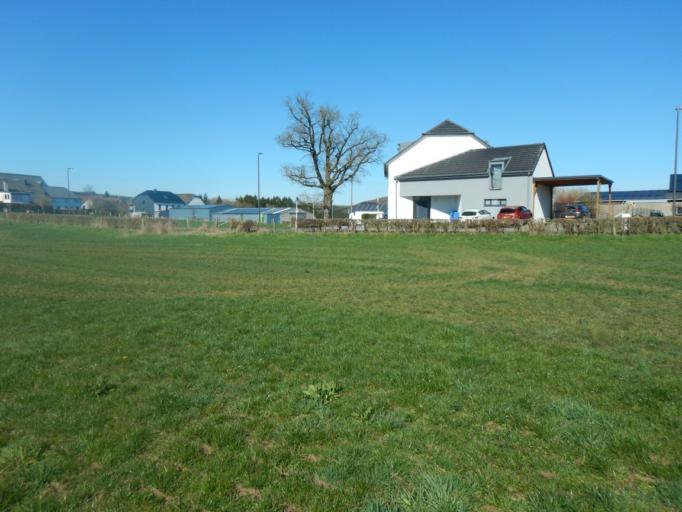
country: LU
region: Diekirch
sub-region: Canton de Wiltz
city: Eschweiler
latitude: 49.9975
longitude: 5.9497
